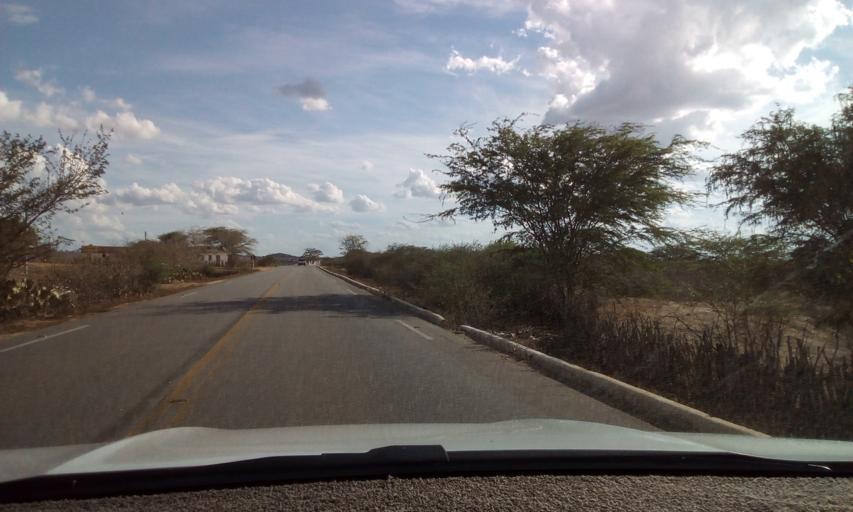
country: BR
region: Paraiba
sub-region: Soledade
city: Soledade
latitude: -6.9429
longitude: -36.3854
